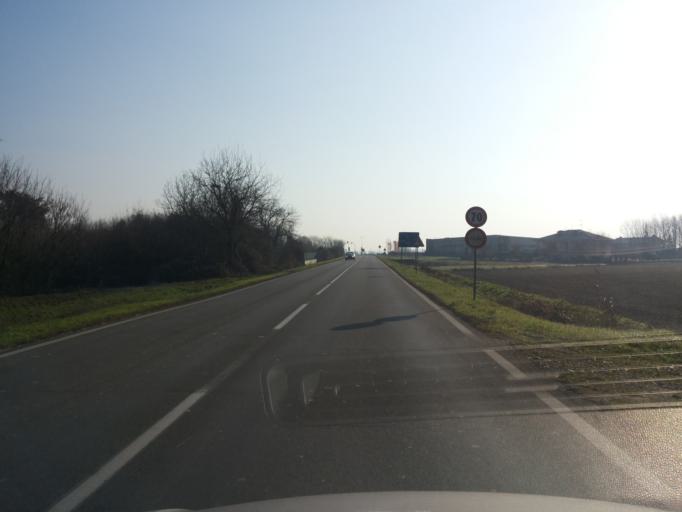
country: IT
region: Piedmont
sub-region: Provincia di Vercelli
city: Caresana
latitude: 45.2177
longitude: 8.5033
